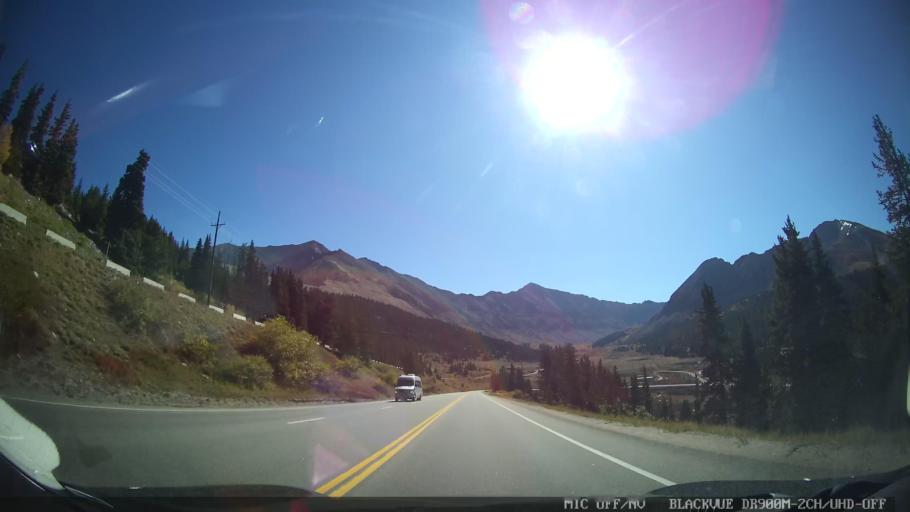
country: US
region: Colorado
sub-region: Lake County
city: Leadville
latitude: 39.3656
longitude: -106.1848
